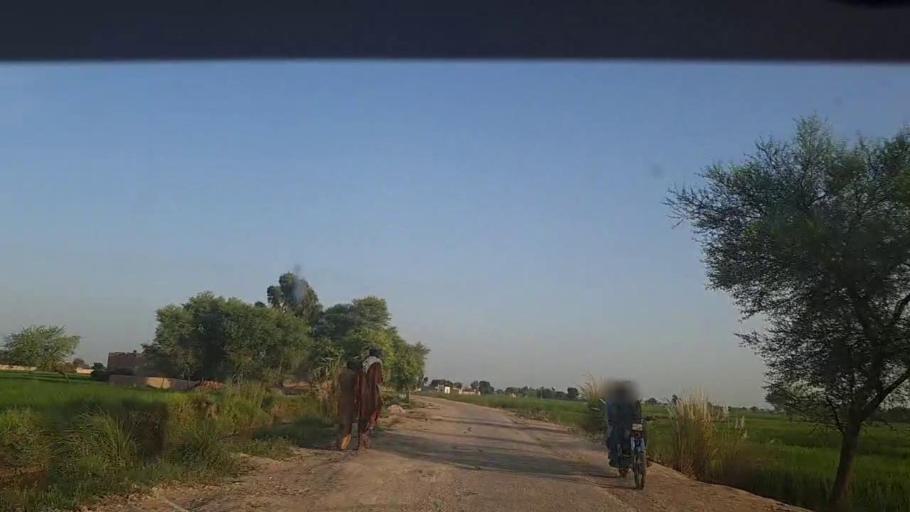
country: PK
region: Sindh
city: Thul
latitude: 28.1175
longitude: 68.8969
